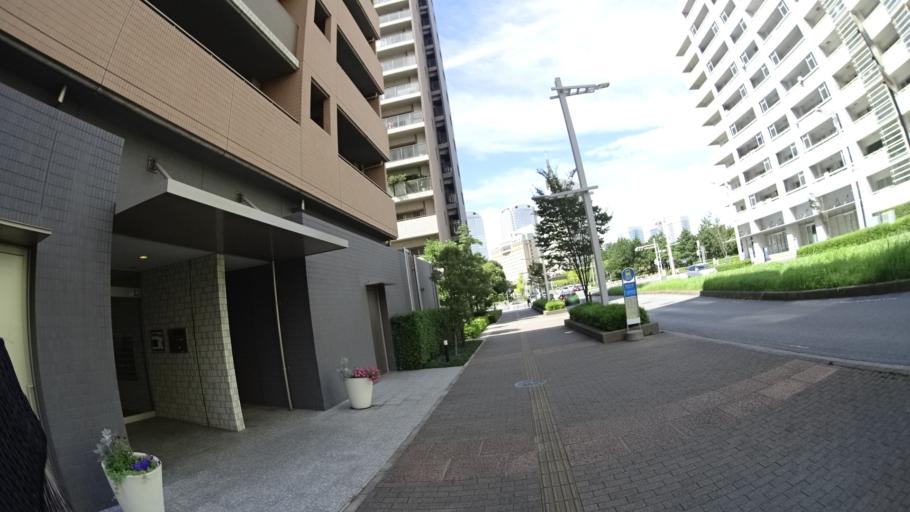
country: JP
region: Chiba
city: Funabashi
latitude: 35.6422
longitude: 140.0417
